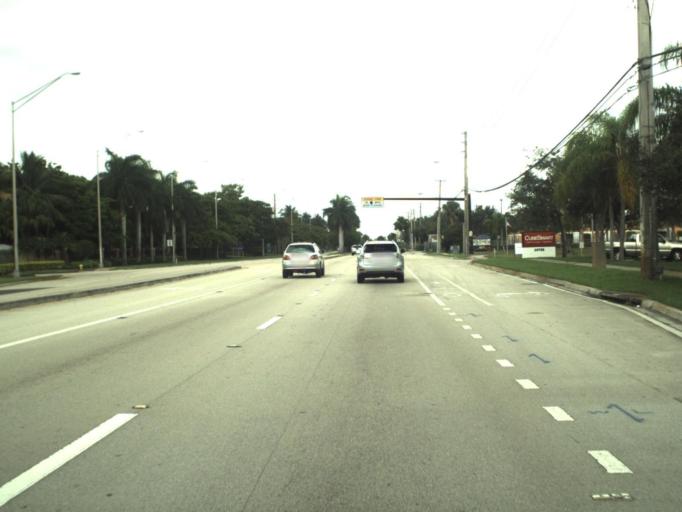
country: US
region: Florida
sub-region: Miami-Dade County
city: Country Club
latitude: 25.9935
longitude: -80.2876
